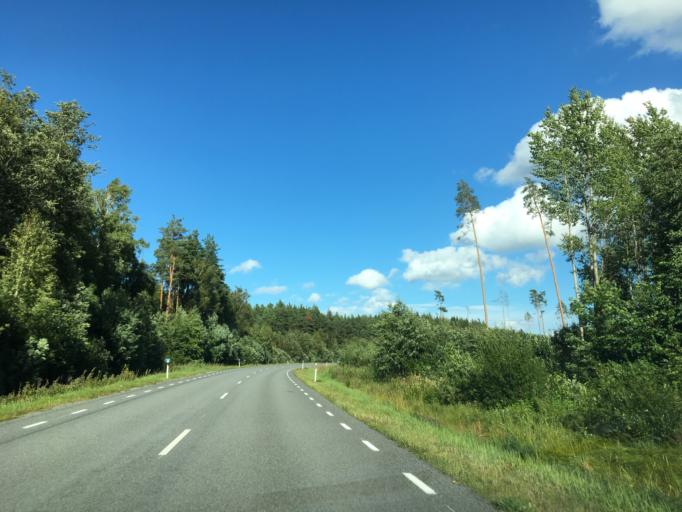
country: EE
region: Paernumaa
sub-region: Vaendra vald (alev)
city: Vandra
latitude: 58.5782
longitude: 25.2254
